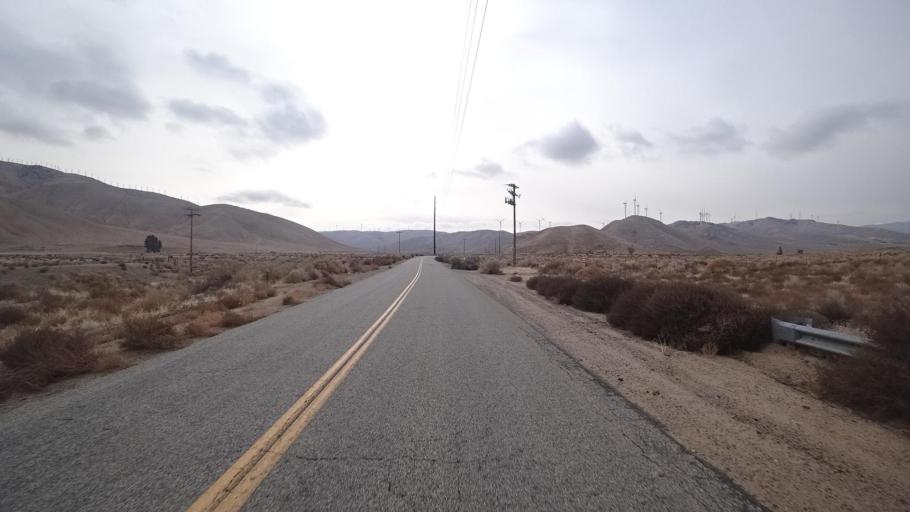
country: US
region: California
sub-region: Kern County
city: Tehachapi
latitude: 35.1247
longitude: -118.3253
